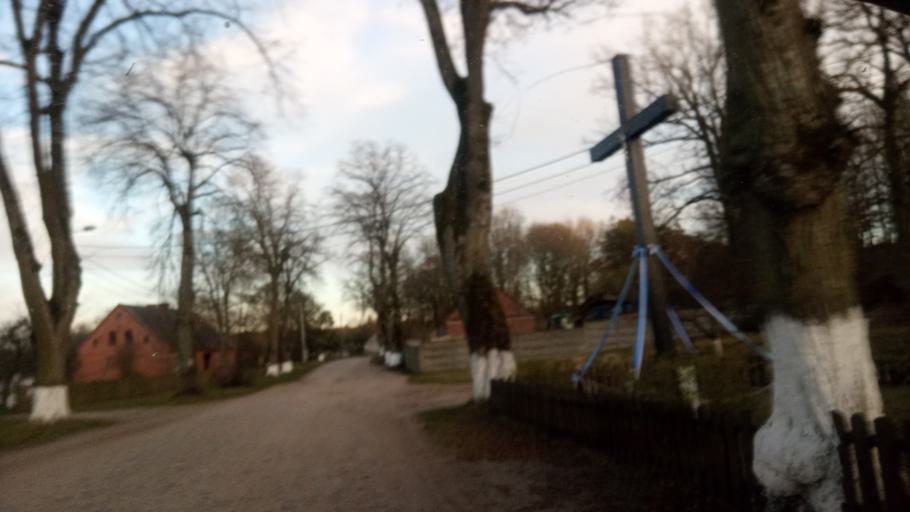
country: PL
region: West Pomeranian Voivodeship
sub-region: Powiat szczecinecki
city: Lubowo
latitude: 53.5511
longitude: 16.3942
